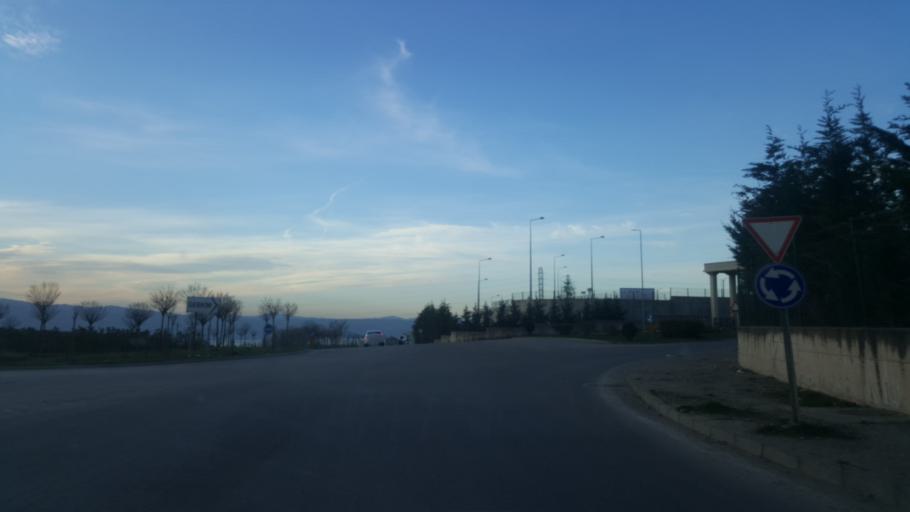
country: TR
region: Kocaeli
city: Tavsancil
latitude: 40.8129
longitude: 29.5670
